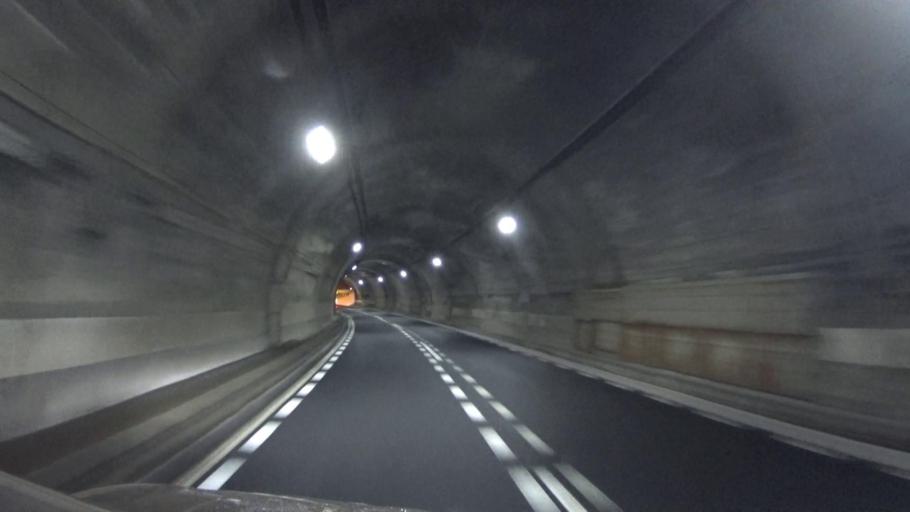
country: JP
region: Hokkaido
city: Otaru
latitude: 43.1633
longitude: 141.0969
